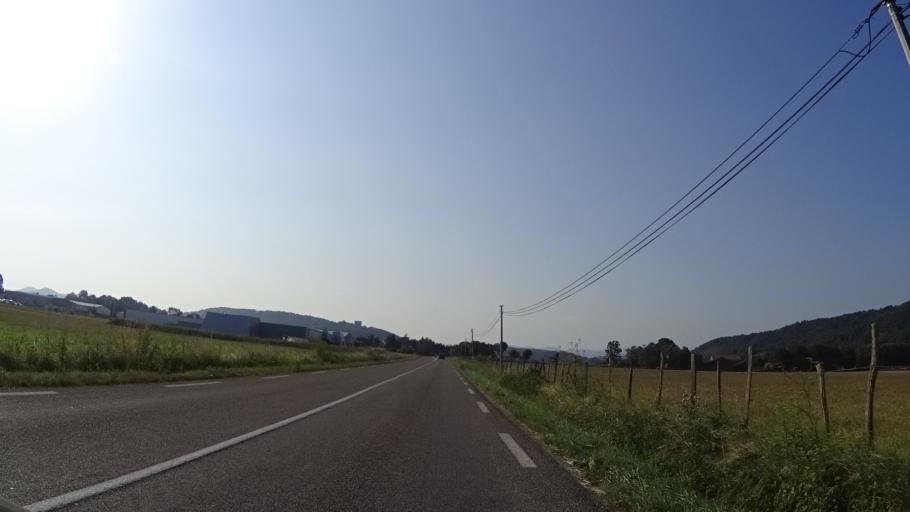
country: FR
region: Midi-Pyrenees
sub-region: Departement de l'Ariege
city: Mirepoix
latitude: 43.0493
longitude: 1.8908
